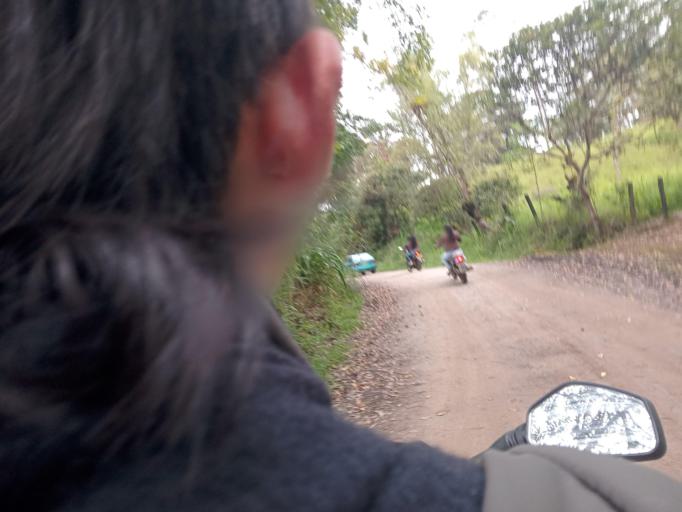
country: CO
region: Cundinamarca
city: Tenza
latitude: 5.1023
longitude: -73.4353
